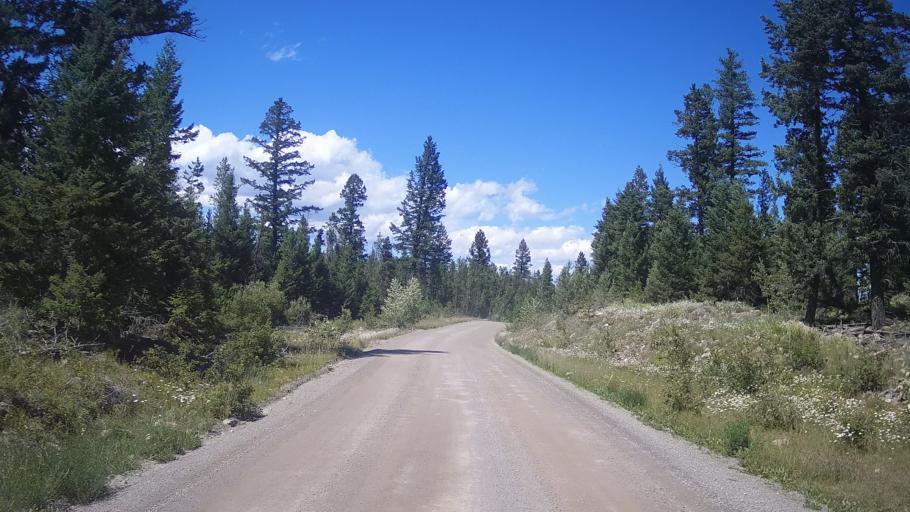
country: CA
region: British Columbia
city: Cache Creek
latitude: 51.1649
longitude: -121.5609
